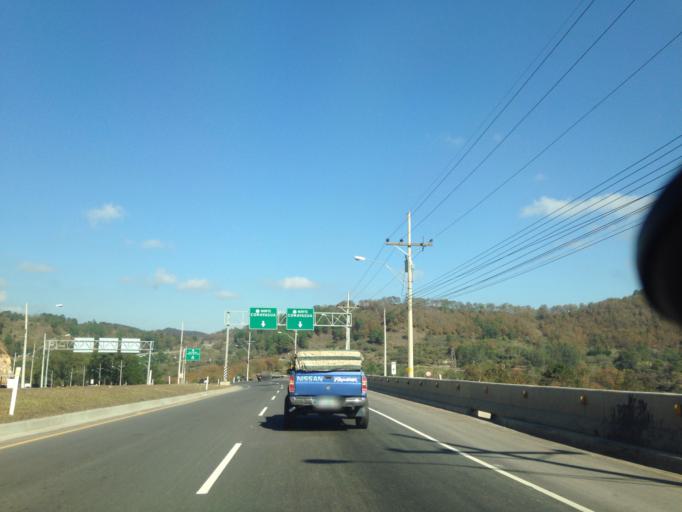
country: HN
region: Francisco Morazan
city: El Lolo
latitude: 14.1379
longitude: -87.2737
